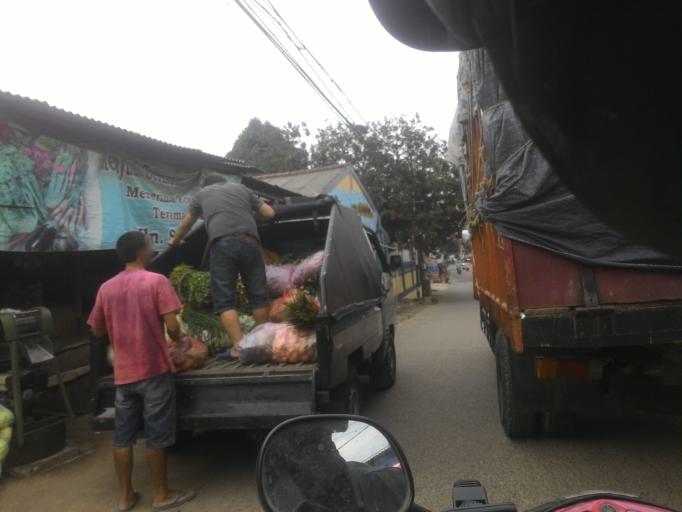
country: ID
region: West Java
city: Depok
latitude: -6.4158
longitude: 106.8419
